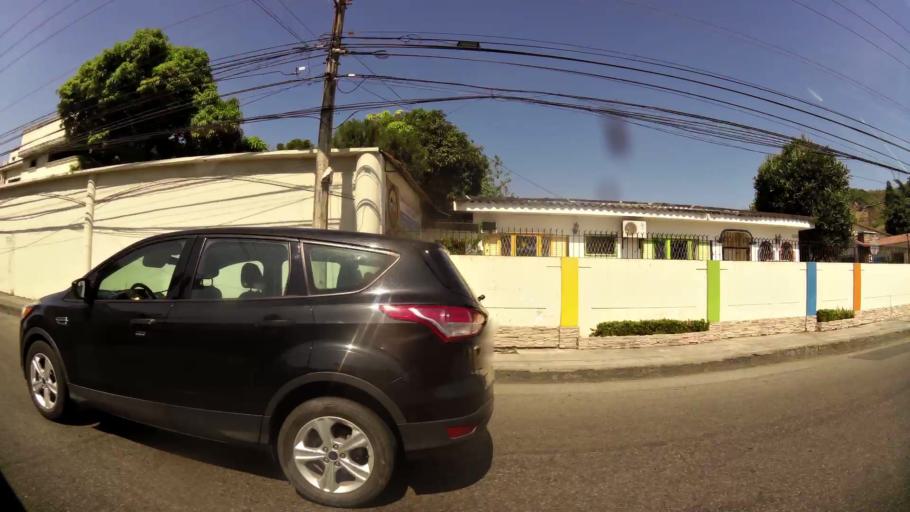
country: EC
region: Guayas
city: Guayaquil
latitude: -2.1665
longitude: -79.9201
